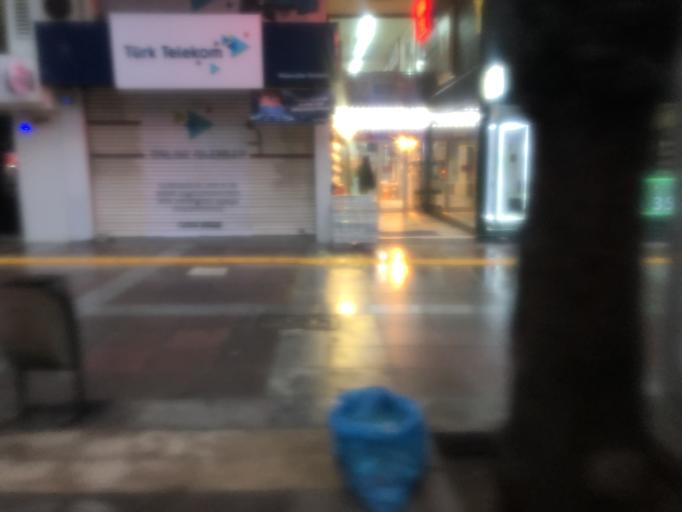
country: TR
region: Ankara
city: Ankara
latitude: 39.9241
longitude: 32.8545
